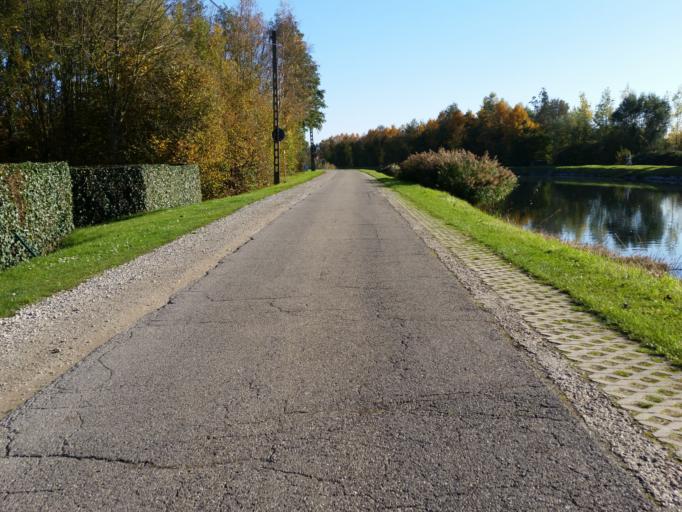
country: BE
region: Flanders
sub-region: Provincie Vlaams-Brabant
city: Herent
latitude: 50.9274
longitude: 4.6844
